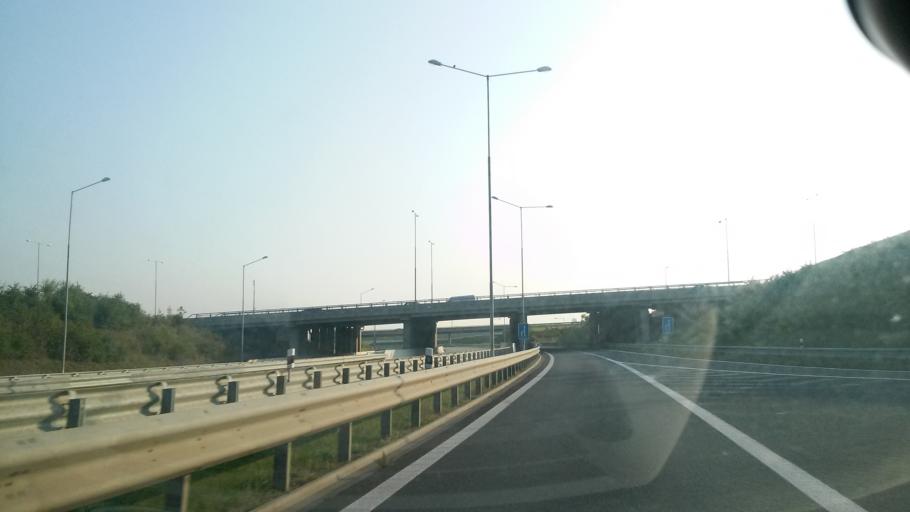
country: CZ
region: Central Bohemia
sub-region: Okres Praha-Vychod
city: Ricany
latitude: 49.9802
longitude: 14.6049
